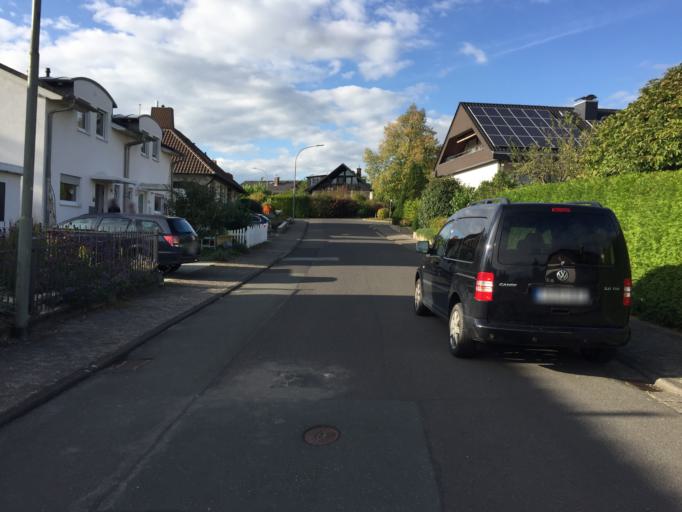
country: DE
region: Hesse
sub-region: Regierungsbezirk Darmstadt
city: Rockenberg
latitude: 50.4647
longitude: 8.7360
